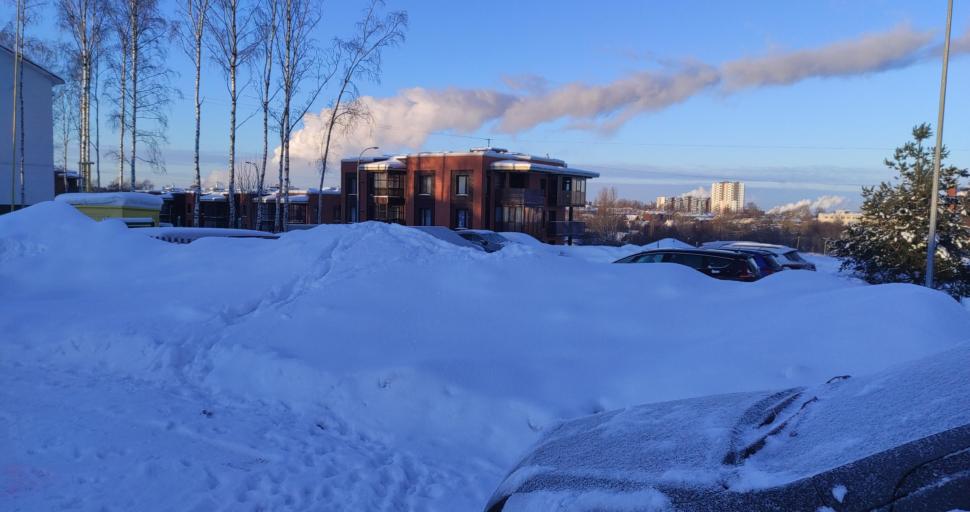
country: RU
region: Republic of Karelia
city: Petrozavodsk
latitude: 61.7882
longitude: 34.3210
